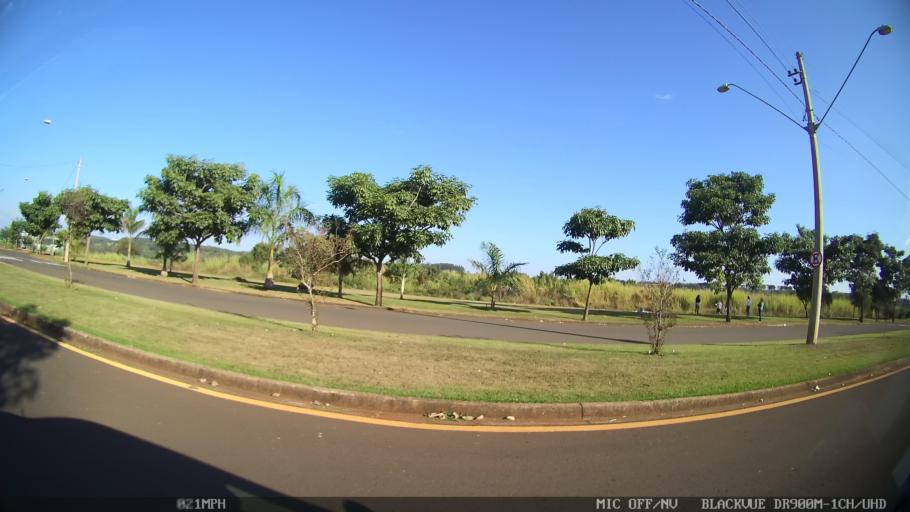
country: BR
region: Sao Paulo
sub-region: Piracicaba
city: Piracicaba
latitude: -22.6951
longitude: -47.6160
